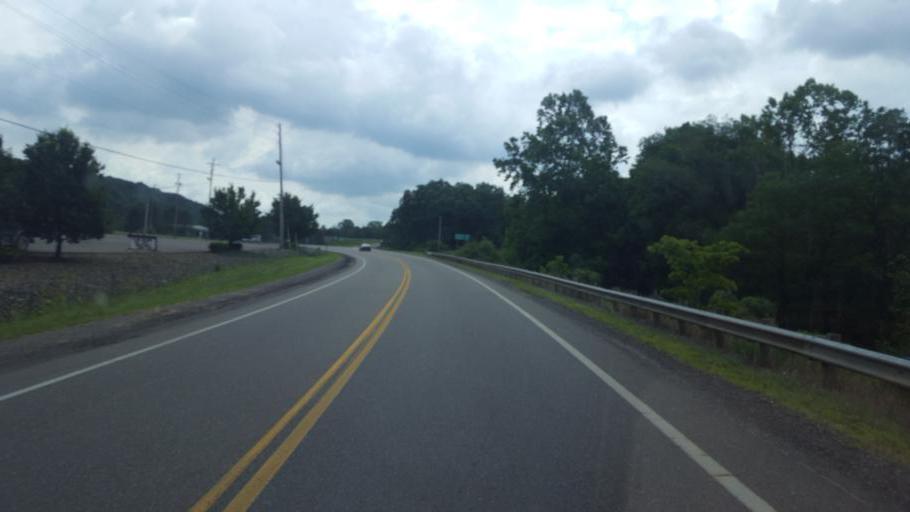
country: US
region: Ohio
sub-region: Columbiana County
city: Lisbon
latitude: 40.7652
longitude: -80.7308
